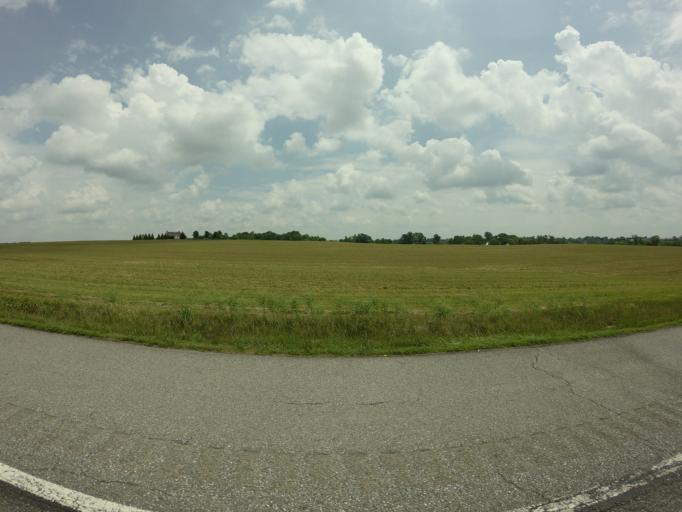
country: US
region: Maryland
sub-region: Frederick County
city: Brunswick
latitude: 39.3462
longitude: -77.6296
